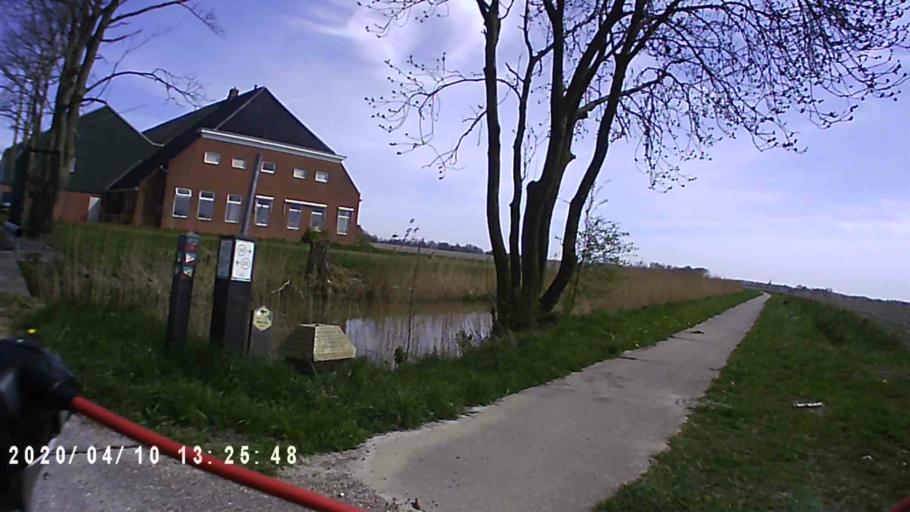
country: NL
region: Groningen
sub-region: Gemeente Zuidhorn
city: Oldehove
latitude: 53.3811
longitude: 6.4231
